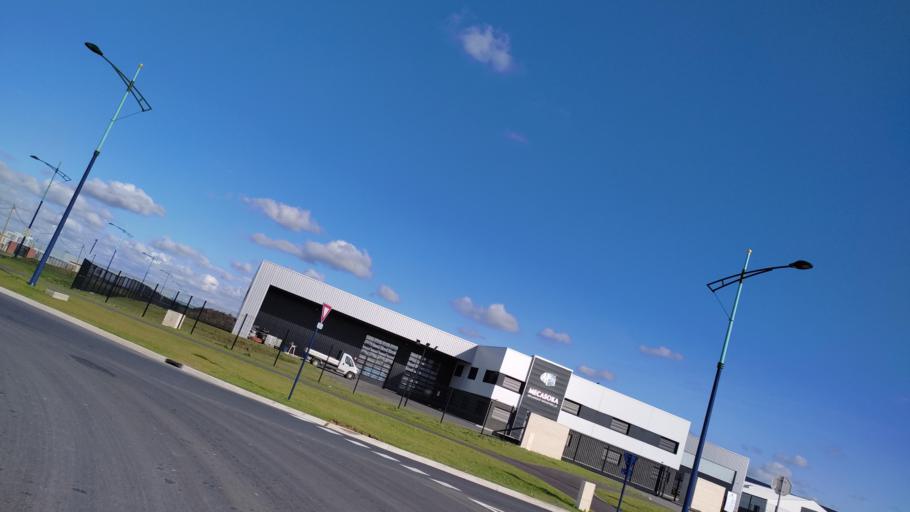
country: FR
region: Nord-Pas-de-Calais
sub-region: Departement du Pas-de-Calais
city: Saint-Laurent-Blangy
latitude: 50.3190
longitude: 2.8244
